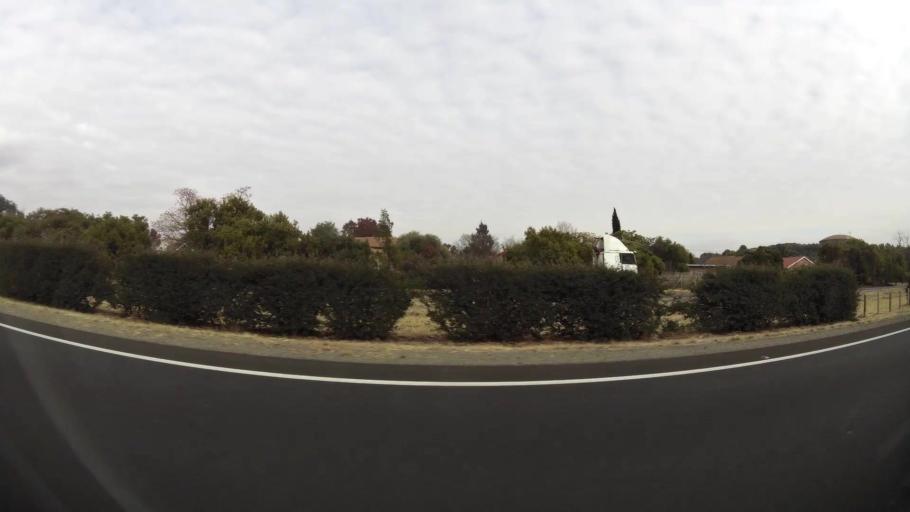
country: ZA
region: Orange Free State
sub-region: Mangaung Metropolitan Municipality
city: Bloemfontein
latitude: -29.1465
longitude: 26.1718
